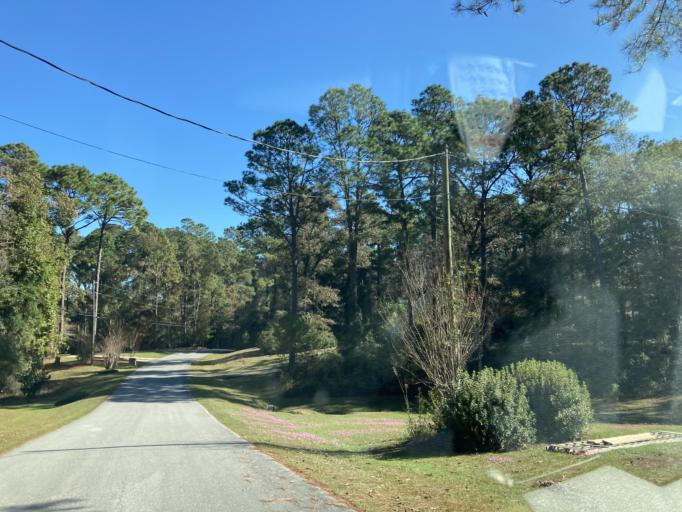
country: US
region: Mississippi
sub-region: Lamar County
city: West Hattiesburg
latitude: 31.3018
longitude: -89.4219
